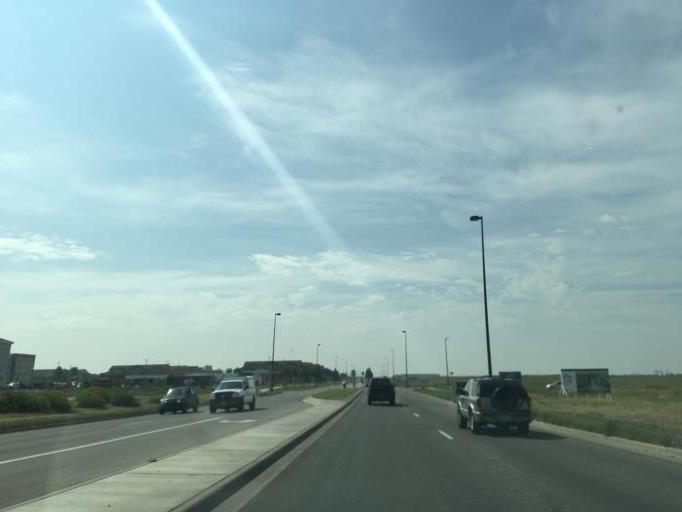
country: US
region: Colorado
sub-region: Adams County
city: Aurora
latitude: 39.8068
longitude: -104.7721
